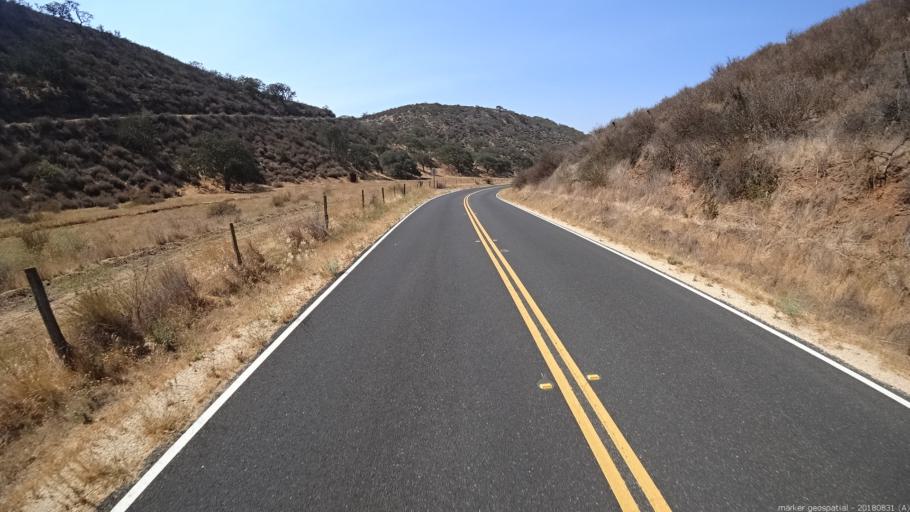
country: US
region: California
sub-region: Monterey County
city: Soledad
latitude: 36.4256
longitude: -121.2303
